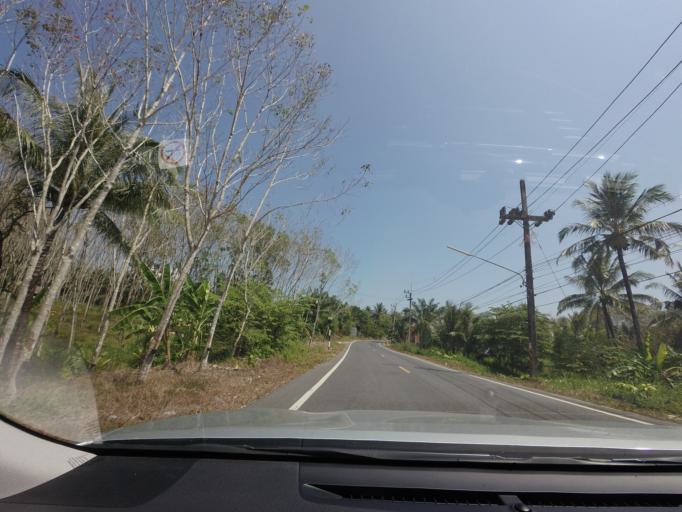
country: TH
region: Phangnga
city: Takua Thung
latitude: 8.2530
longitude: 98.4113
